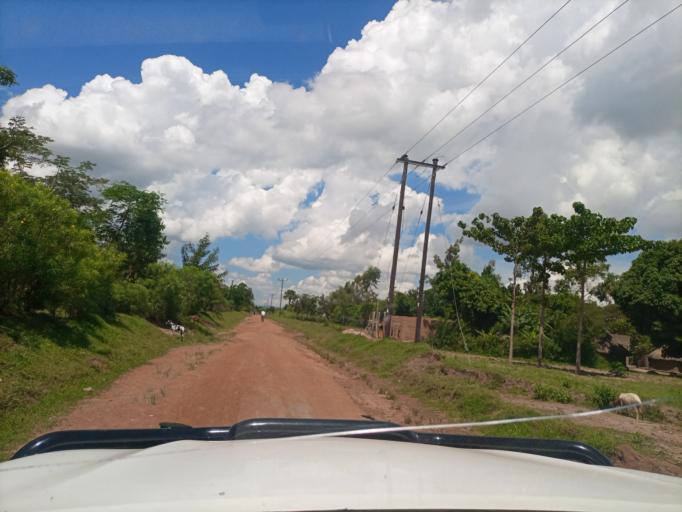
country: UG
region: Eastern Region
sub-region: Tororo District
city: Tororo
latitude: 0.6522
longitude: 33.9978
